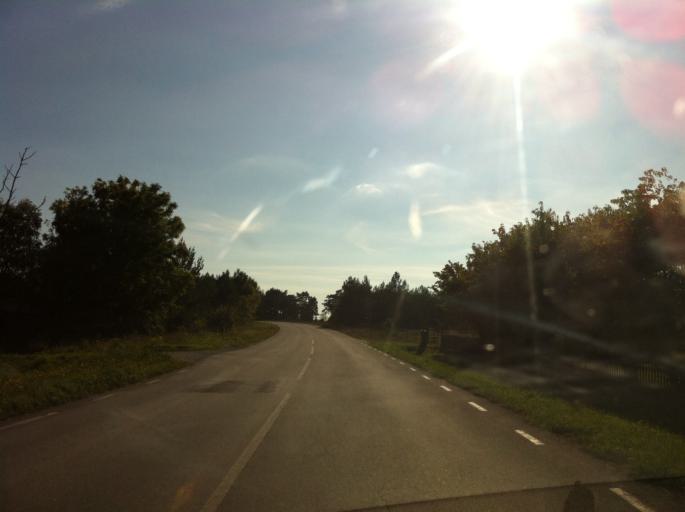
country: SE
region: Gotland
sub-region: Gotland
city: Slite
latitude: 57.9008
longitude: 19.0941
